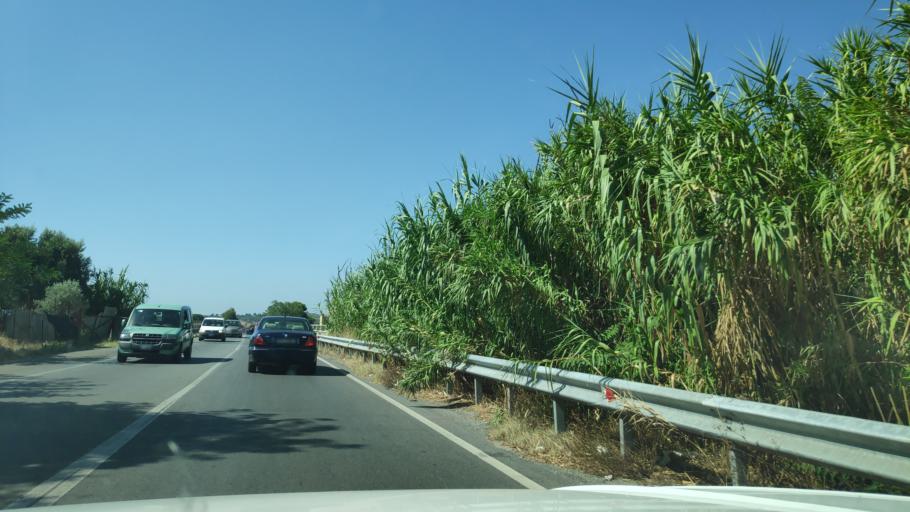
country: IT
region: Calabria
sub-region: Provincia di Reggio Calabria
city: Bovalino
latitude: 38.1374
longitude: 16.1650
